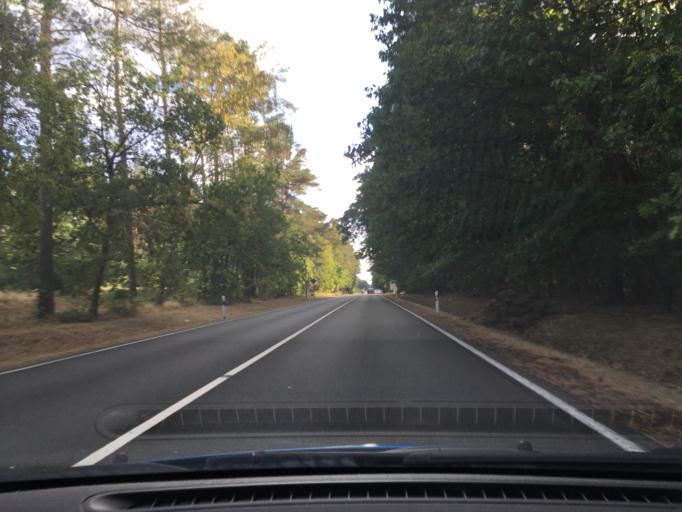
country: DE
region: Mecklenburg-Vorpommern
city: Gross Laasch
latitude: 53.3482
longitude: 11.5288
